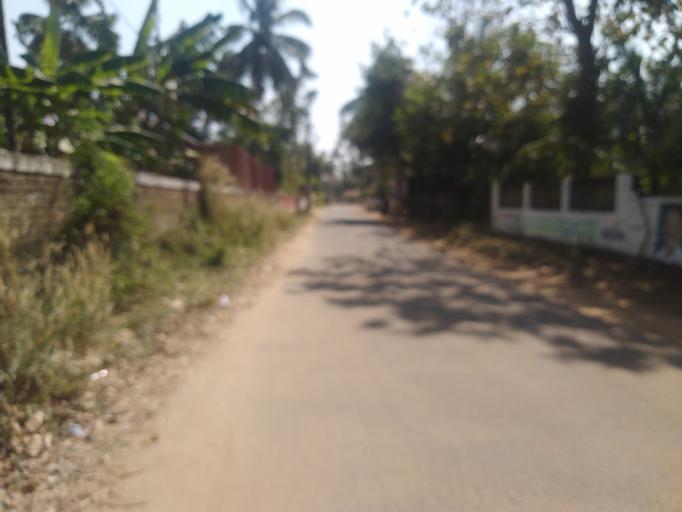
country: IN
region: Kerala
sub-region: Thrissur District
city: Trichur
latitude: 10.4884
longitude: 76.2834
